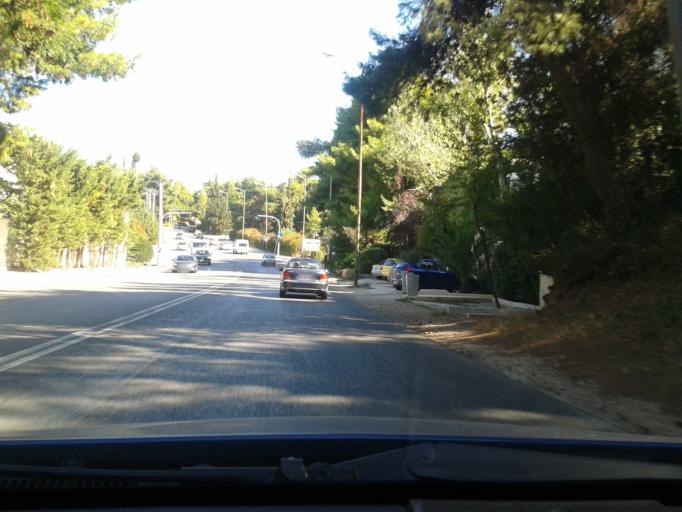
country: GR
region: Attica
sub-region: Nomarchia Athinas
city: Ekali
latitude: 38.1113
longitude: 23.8439
